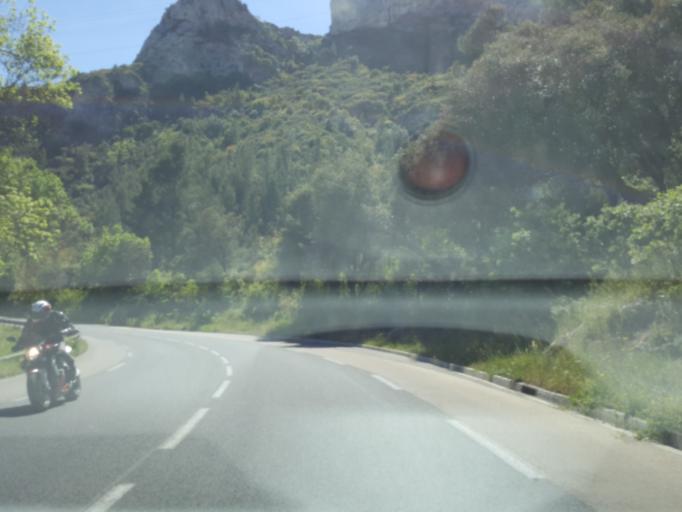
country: FR
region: Provence-Alpes-Cote d'Azur
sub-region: Departement des Bouches-du-Rhone
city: Roquevaire
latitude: 43.3602
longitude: 5.6087
